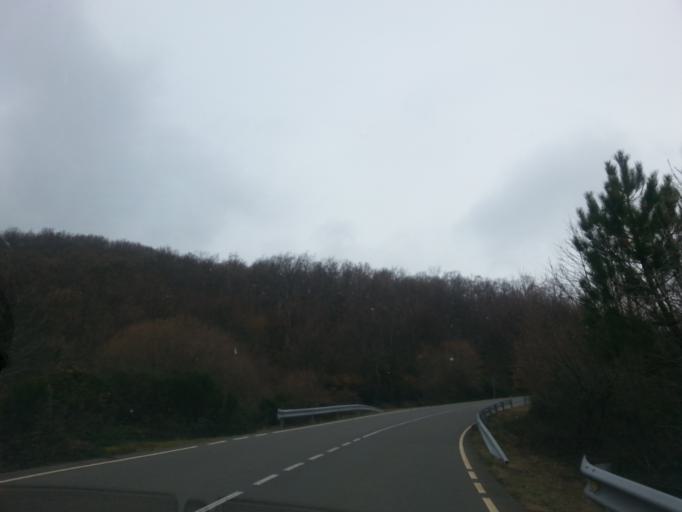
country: ES
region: Castille and Leon
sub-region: Provincia de Salamanca
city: Madronal
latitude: 40.4686
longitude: -6.0790
